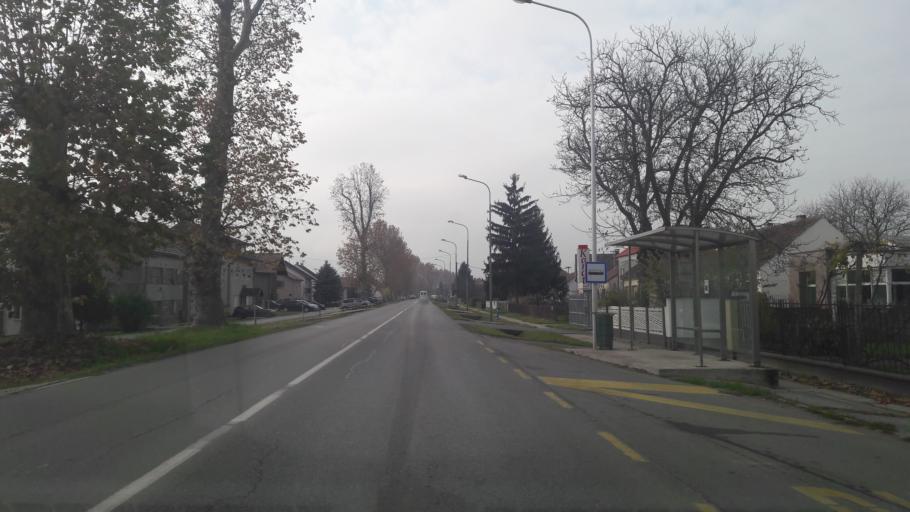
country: HR
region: Osjecko-Baranjska
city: Visnjevac
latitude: 45.5346
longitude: 18.6328
